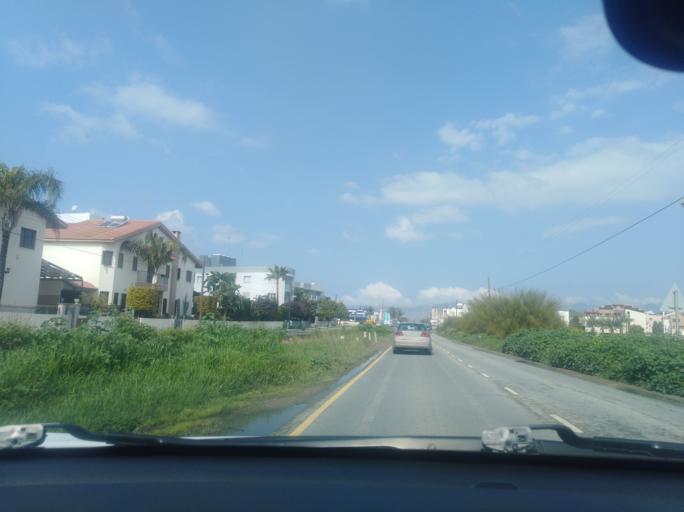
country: CY
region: Lefkosia
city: Nicosia
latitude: 35.1666
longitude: 33.3985
